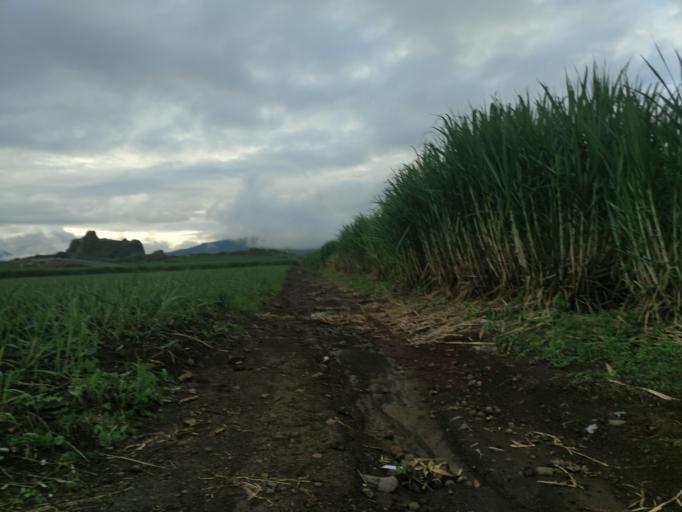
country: MX
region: Nayarit
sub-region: Tepic
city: La Corregidora
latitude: 21.4736
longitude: -104.8056
